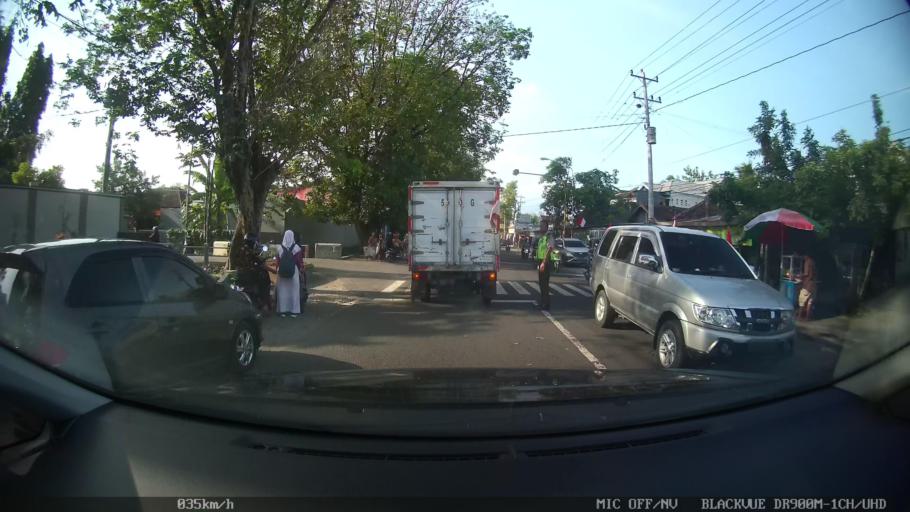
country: ID
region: Daerah Istimewa Yogyakarta
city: Bantul
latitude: -7.8979
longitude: 110.3228
